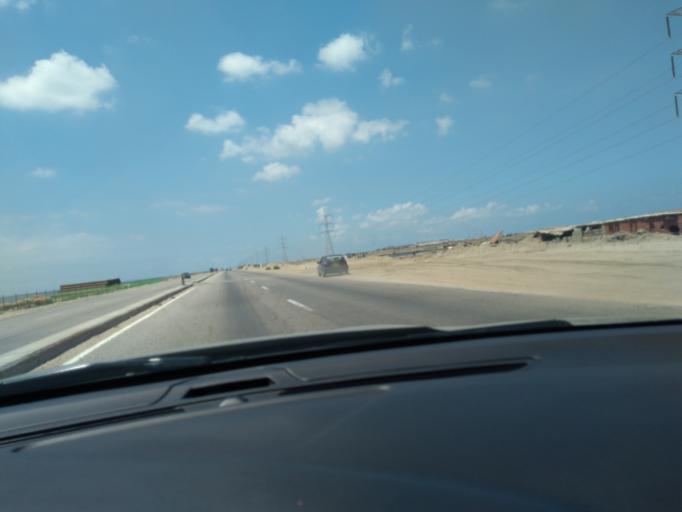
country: EG
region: Muhafazat ad Daqahliyah
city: Al Matariyah
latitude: 31.3103
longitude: 32.1305
